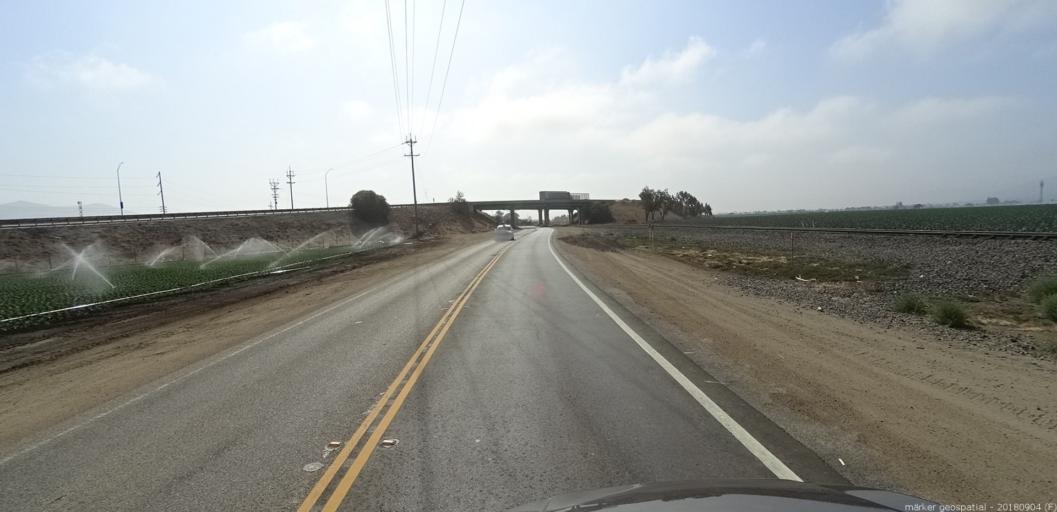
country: US
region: California
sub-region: Monterey County
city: Soledad
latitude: 36.4328
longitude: -121.3391
